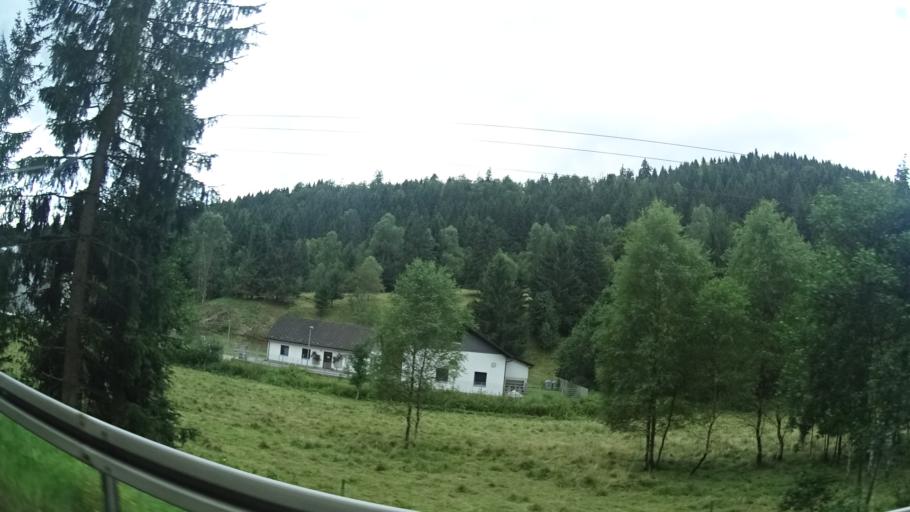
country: DE
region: Bavaria
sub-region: Upper Franconia
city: Tettau
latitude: 50.4355
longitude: 11.2677
